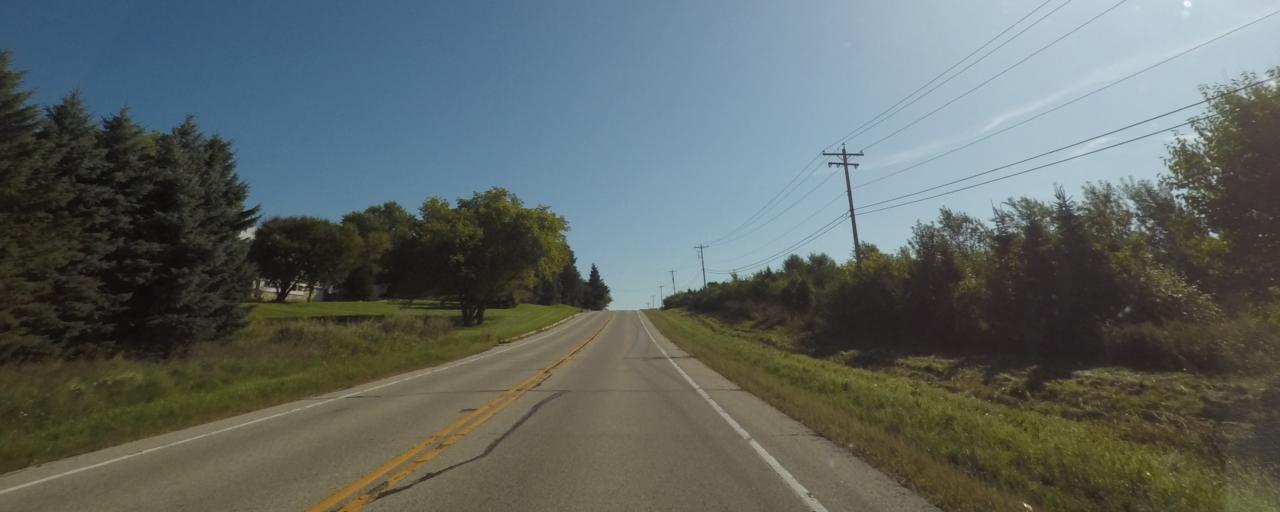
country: US
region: Wisconsin
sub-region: Waukesha County
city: Dousman
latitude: 43.0210
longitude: -88.5551
